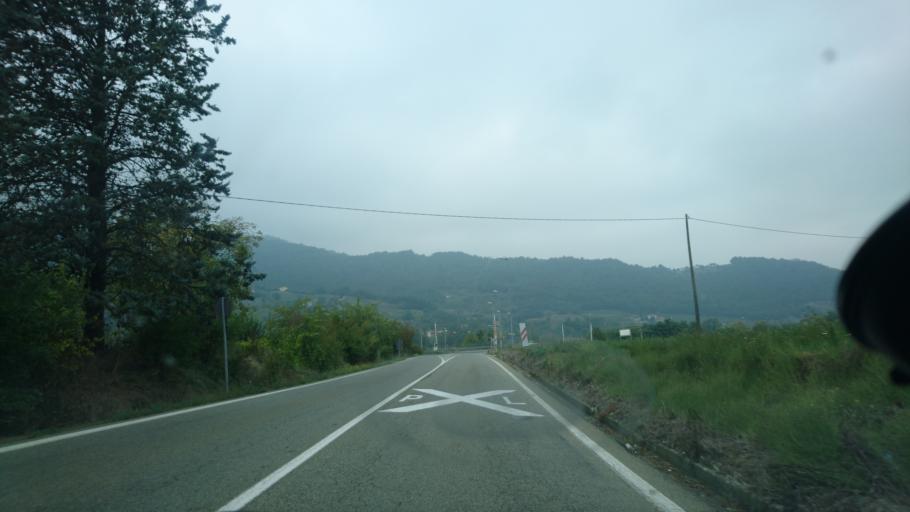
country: IT
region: Piedmont
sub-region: Provincia di Alessandria
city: Ponti
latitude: 44.6131
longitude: 8.3500
